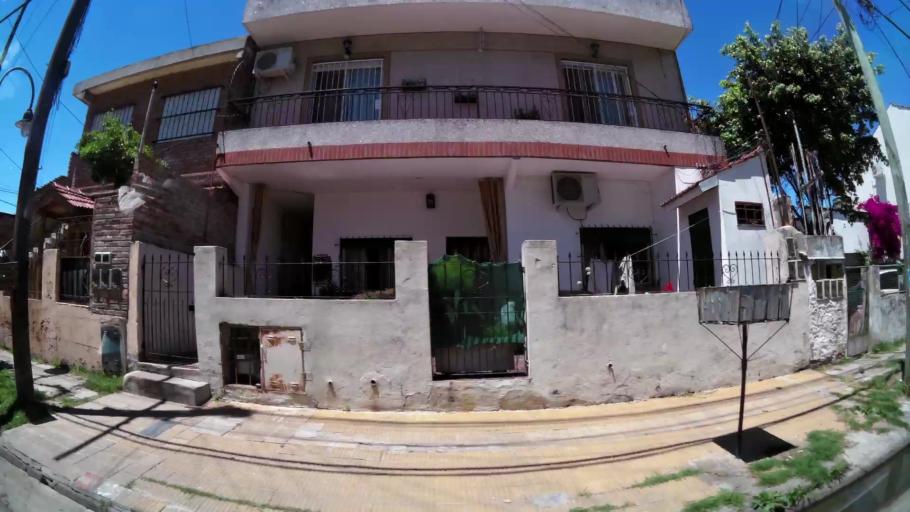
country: AR
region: Buenos Aires
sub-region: Partido de Tigre
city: Tigre
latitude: -34.4504
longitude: -58.5596
